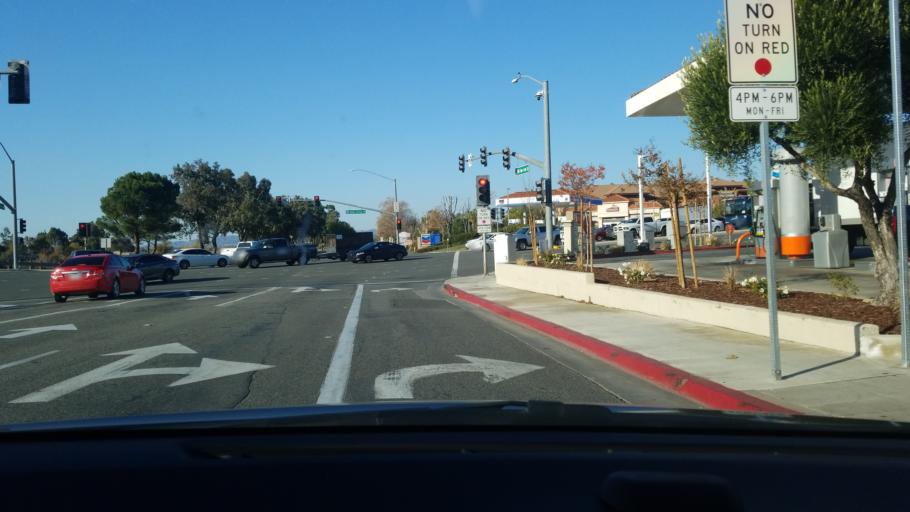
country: US
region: California
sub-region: Riverside County
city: Temecula
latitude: 33.4988
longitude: -117.1536
